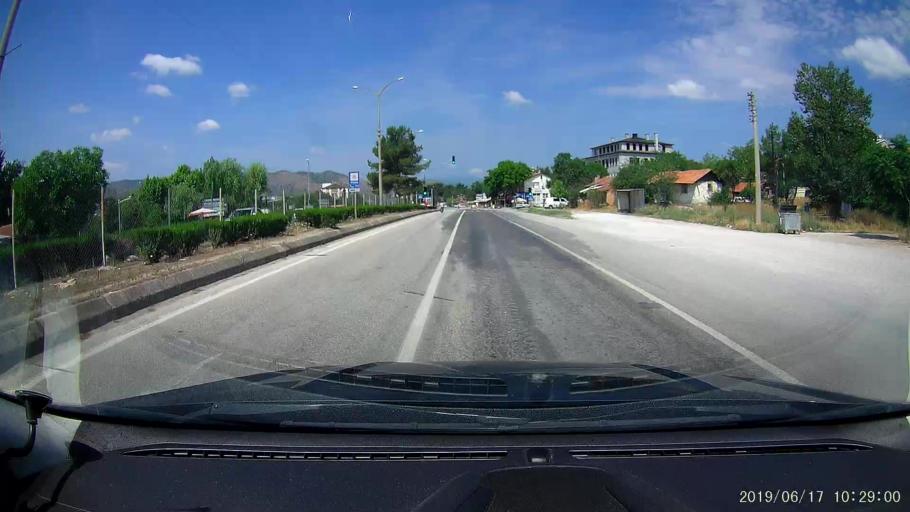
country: TR
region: Corum
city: Osmancik
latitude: 40.9797
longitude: 34.8001
